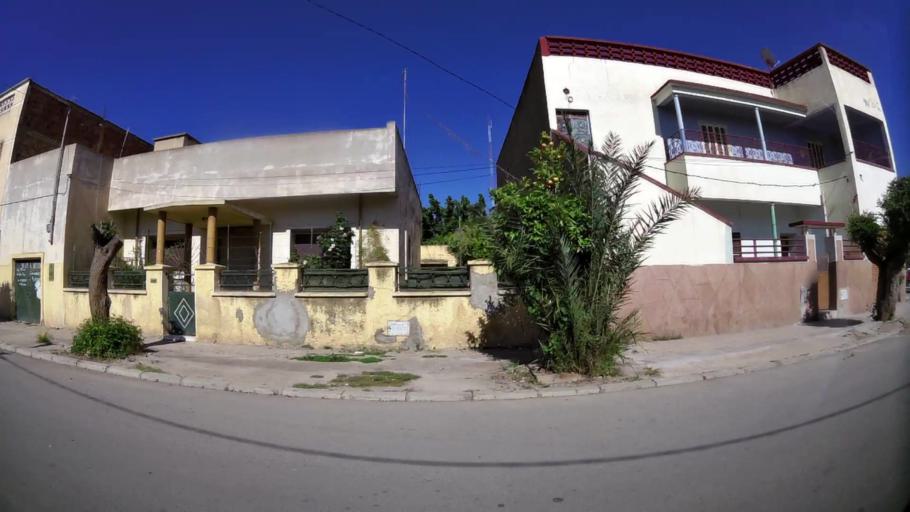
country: MA
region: Oriental
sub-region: Oujda-Angad
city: Oujda
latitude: 34.6882
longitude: -1.9220
